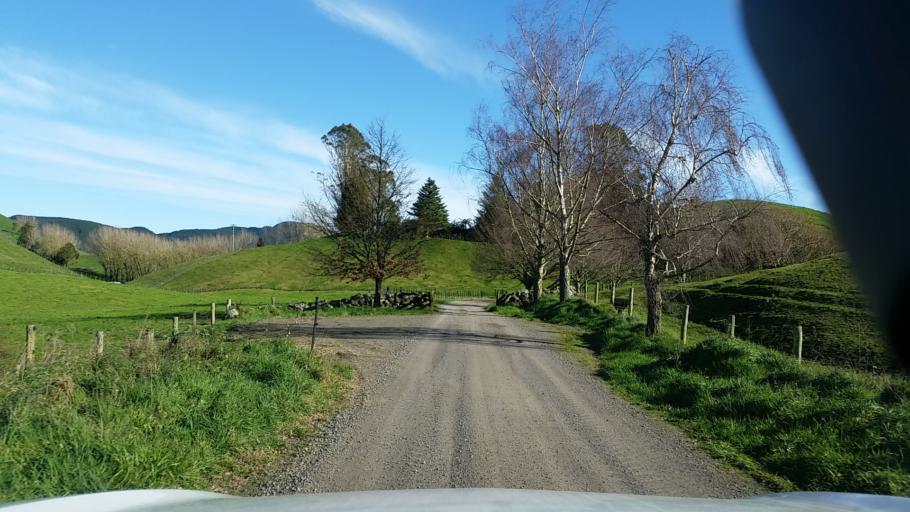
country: NZ
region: Waikato
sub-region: Taupo District
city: Taupo
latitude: -38.4300
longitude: 176.1542
